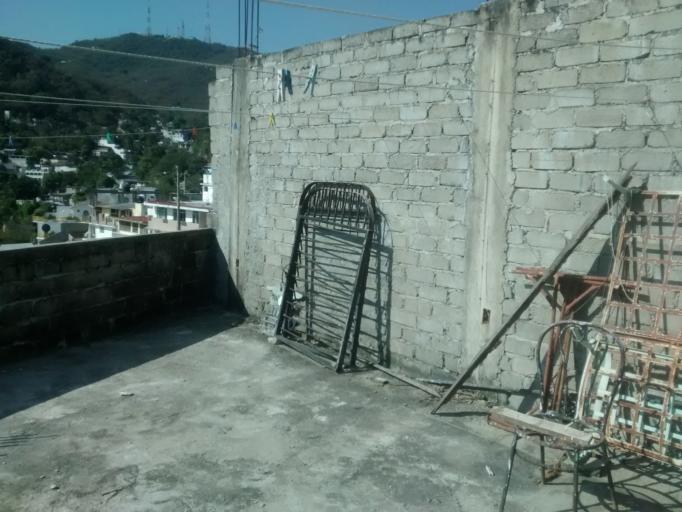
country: MX
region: Guerrero
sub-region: Acapulco de Juarez
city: Colonia Alborada
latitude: 16.8577
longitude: -99.8430
